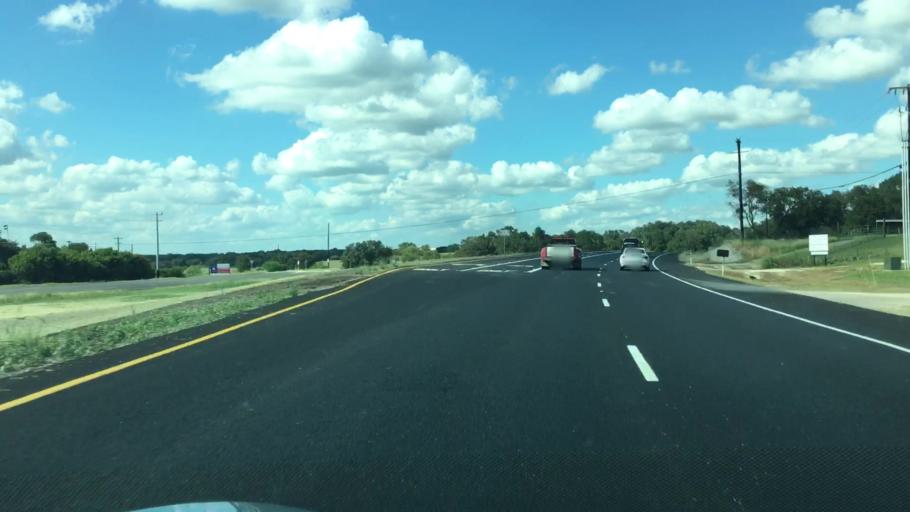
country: US
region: Texas
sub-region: Comal County
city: Canyon Lake
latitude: 29.8947
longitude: -98.4098
